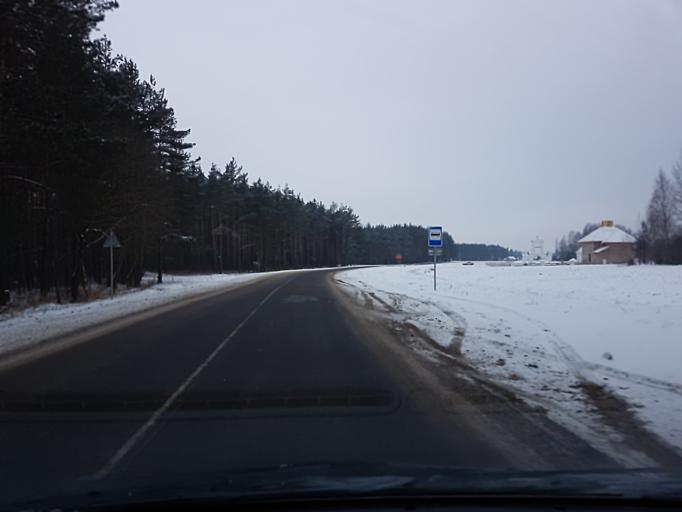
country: BY
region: Minsk
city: Rakaw
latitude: 53.9686
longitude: 27.0824
